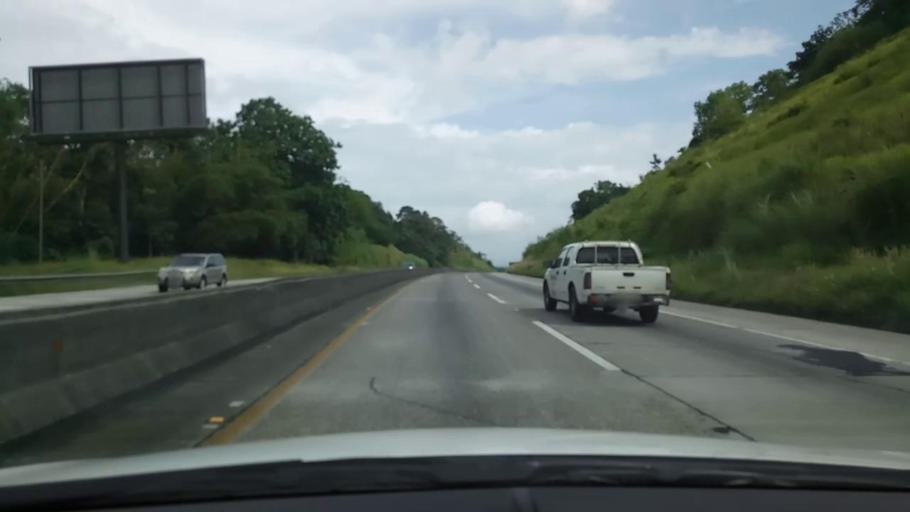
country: PA
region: Colon
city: Quebrada Bonita Adentro
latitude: 9.2836
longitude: -79.7359
